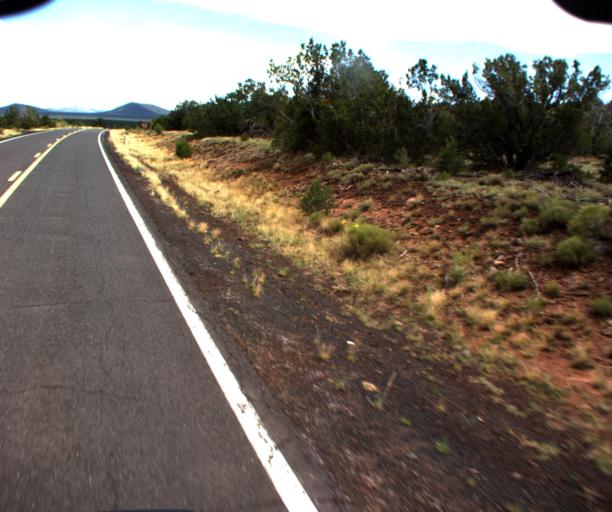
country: US
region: Arizona
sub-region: Coconino County
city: Parks
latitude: 35.5545
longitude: -111.8698
